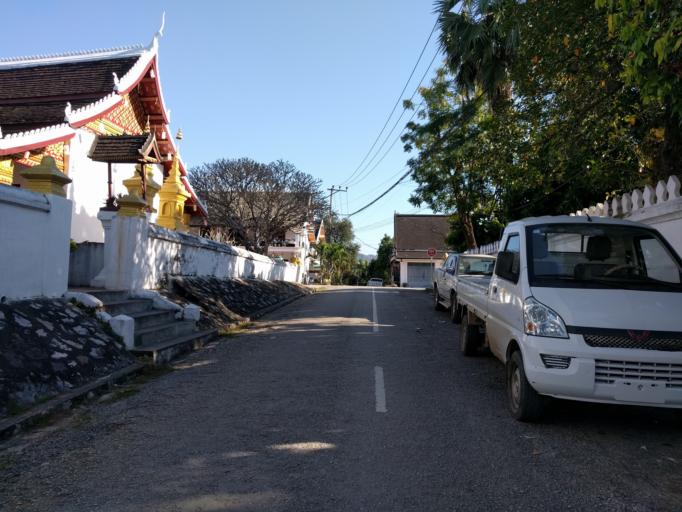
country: LA
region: Louangphabang
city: Louangphabang
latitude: 19.8959
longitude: 102.1419
